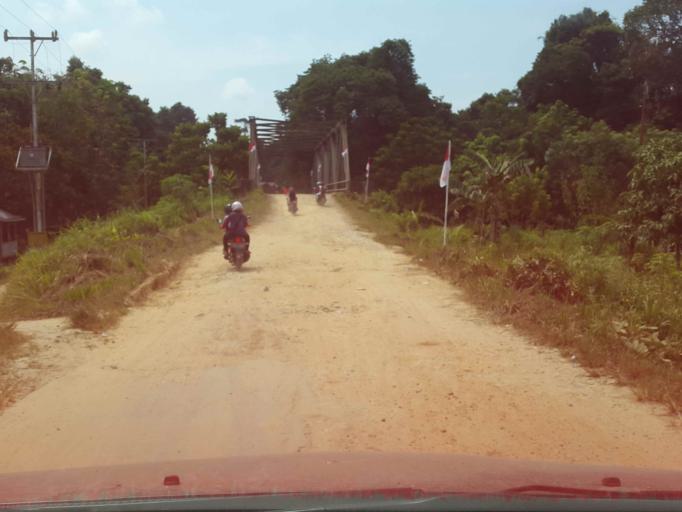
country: MY
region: Sarawak
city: Simanggang
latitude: 0.8405
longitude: 111.7468
